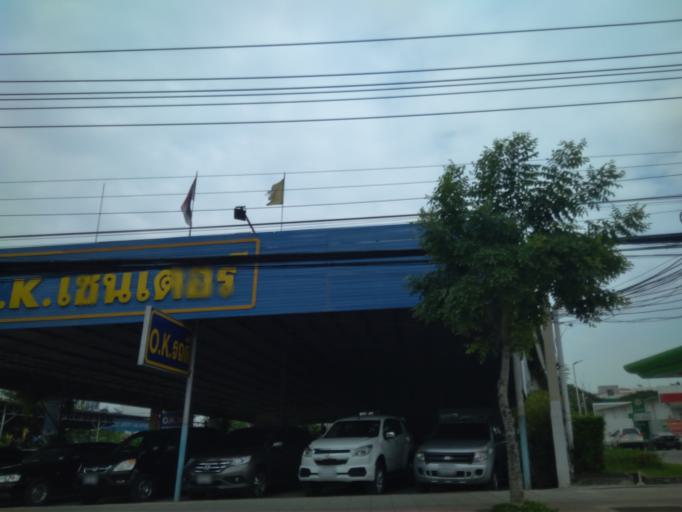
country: TH
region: Bangkok
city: Suan Luang
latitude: 13.7047
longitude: 100.6457
